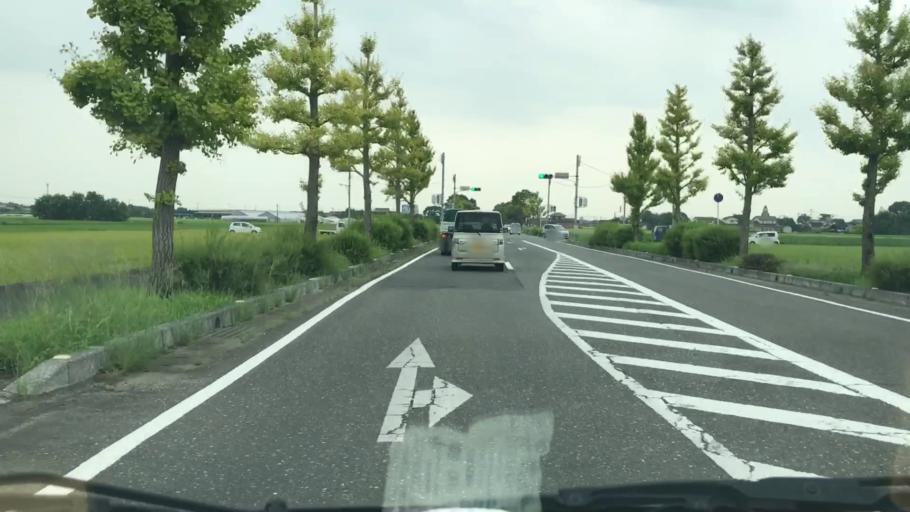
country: JP
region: Saga Prefecture
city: Saga-shi
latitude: 33.2293
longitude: 130.3061
